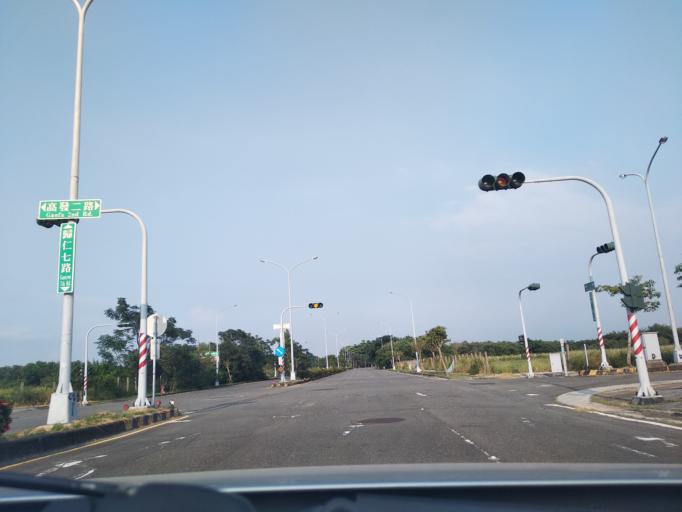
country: TW
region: Taiwan
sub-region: Tainan
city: Tainan
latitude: 22.9281
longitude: 120.2887
